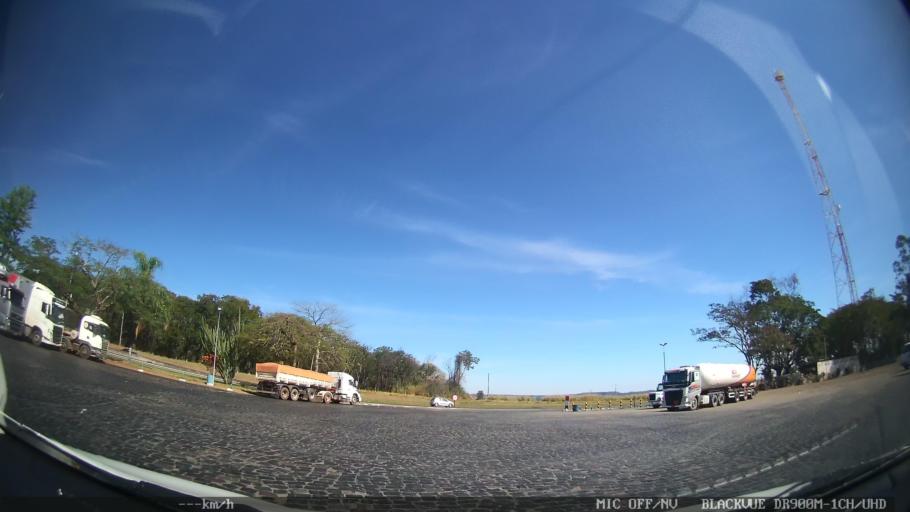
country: BR
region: Sao Paulo
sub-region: Santa Rita Do Passa Quatro
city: Santa Rita do Passa Quatro
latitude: -21.7748
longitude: -47.5394
